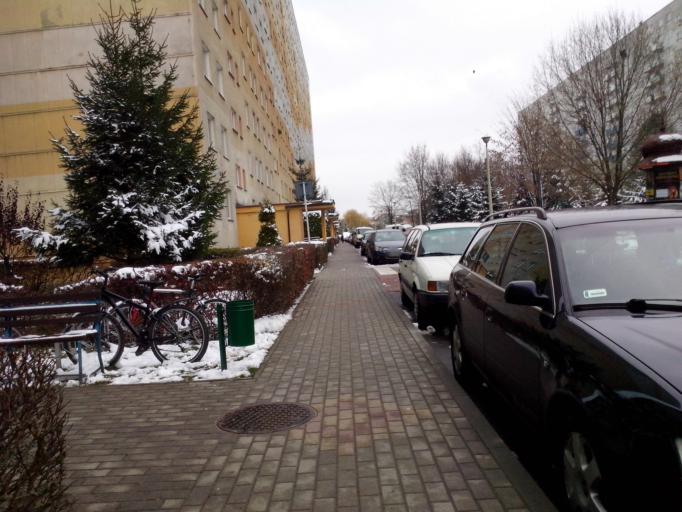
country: PL
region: Subcarpathian Voivodeship
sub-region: Rzeszow
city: Rzeszow
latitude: 50.0220
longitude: 22.0103
